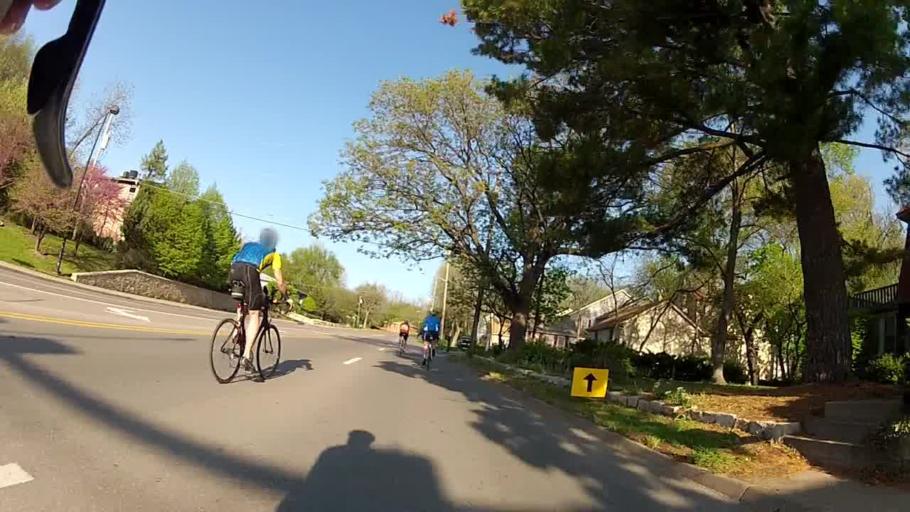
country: US
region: Kansas
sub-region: Riley County
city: Manhattan
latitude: 39.1860
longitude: -96.5890
